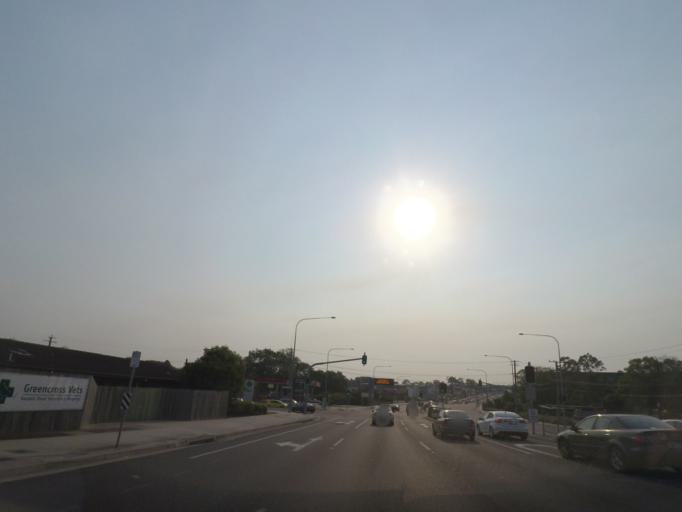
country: AU
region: Queensland
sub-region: Brisbane
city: Upper Mount Gravatt
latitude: -27.5618
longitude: 153.0753
